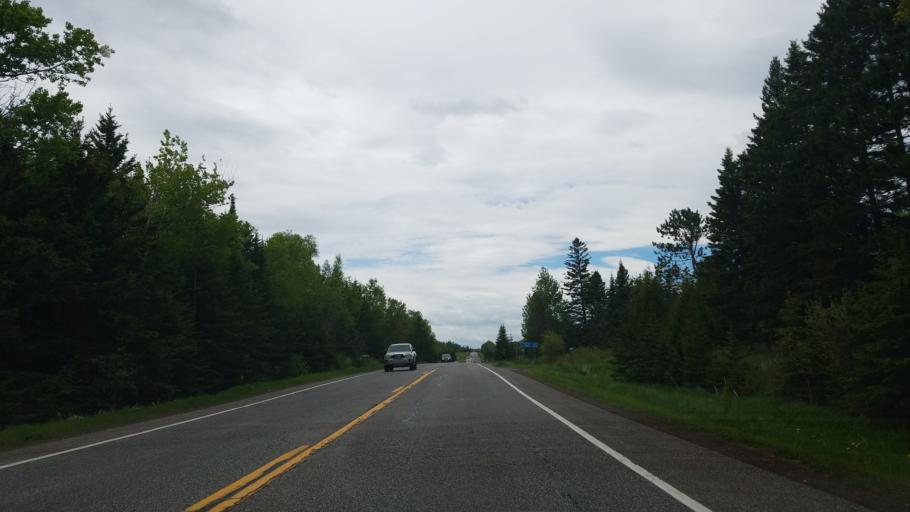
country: US
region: Minnesota
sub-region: Lake County
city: Two Harbors
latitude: 47.0402
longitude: -91.6412
